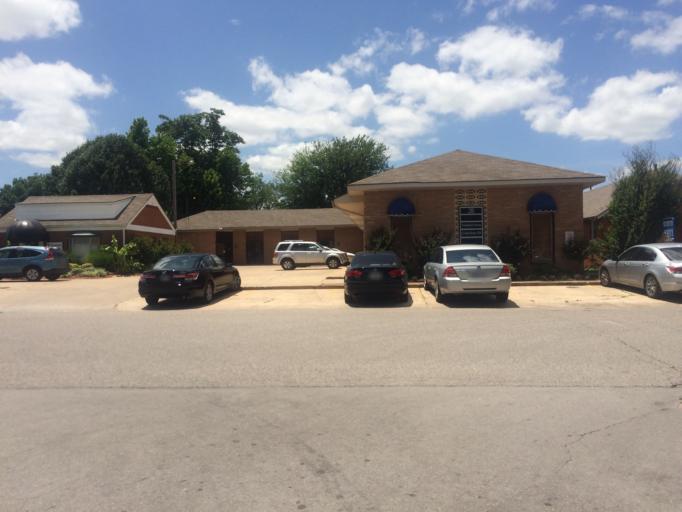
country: US
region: Oklahoma
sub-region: Cleveland County
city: Norman
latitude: 35.2143
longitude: -97.4436
